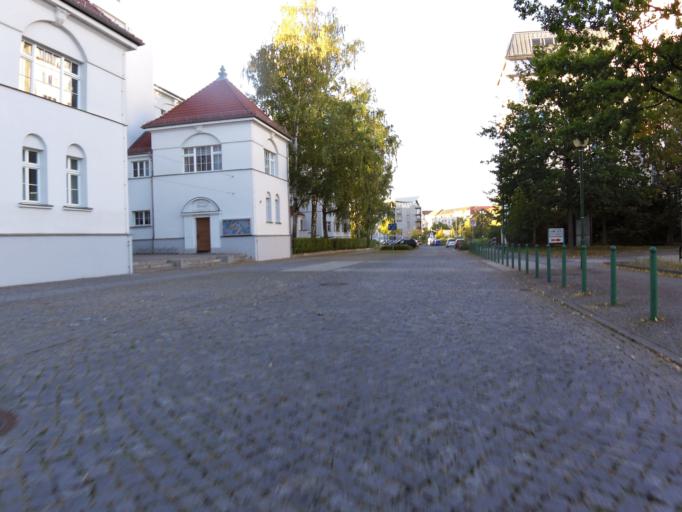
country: DE
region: Saxony
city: Leipzig
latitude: 51.3279
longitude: 12.3987
